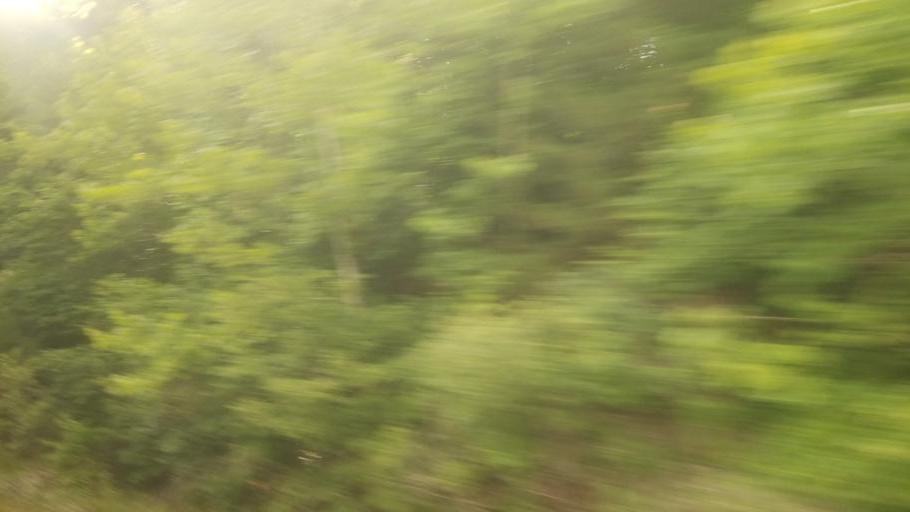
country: US
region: Kansas
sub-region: Johnson County
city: De Soto
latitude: 38.9881
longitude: -94.9100
